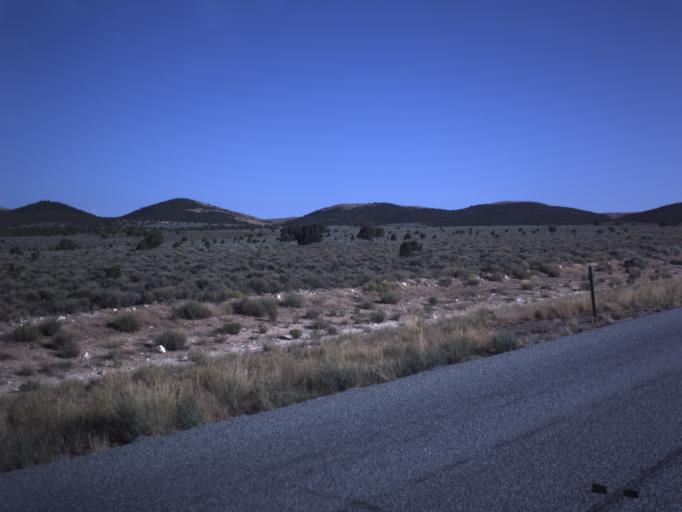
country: US
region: Utah
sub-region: Iron County
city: Parowan
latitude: 38.0241
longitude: -112.9981
